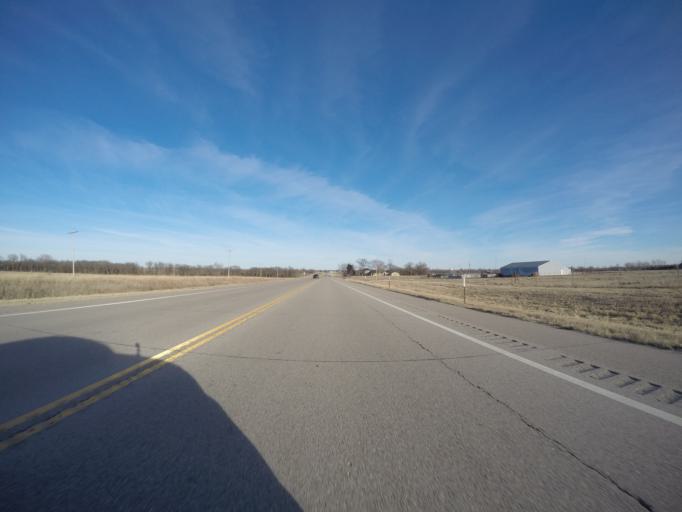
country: US
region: Kansas
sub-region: Marion County
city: Peabody
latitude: 38.1746
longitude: -97.1328
